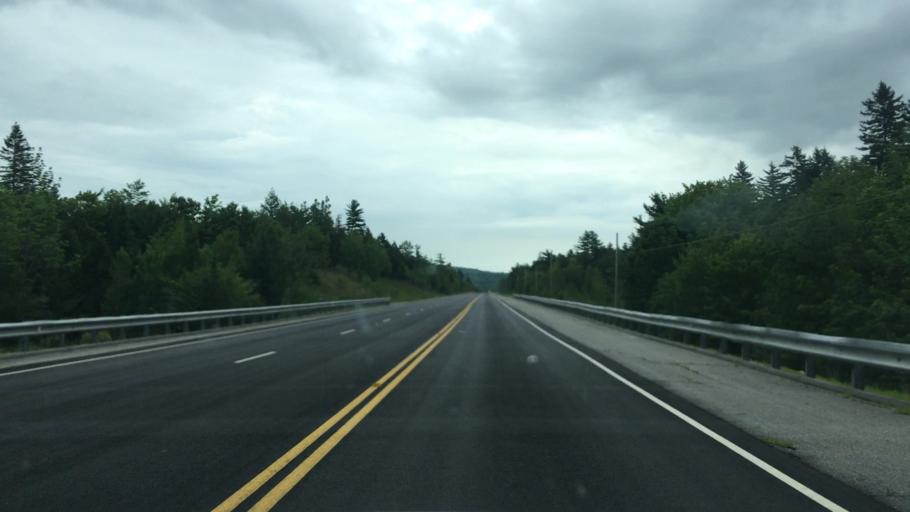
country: US
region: Maine
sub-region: Washington County
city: Cherryfield
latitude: 44.8752
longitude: -67.8960
